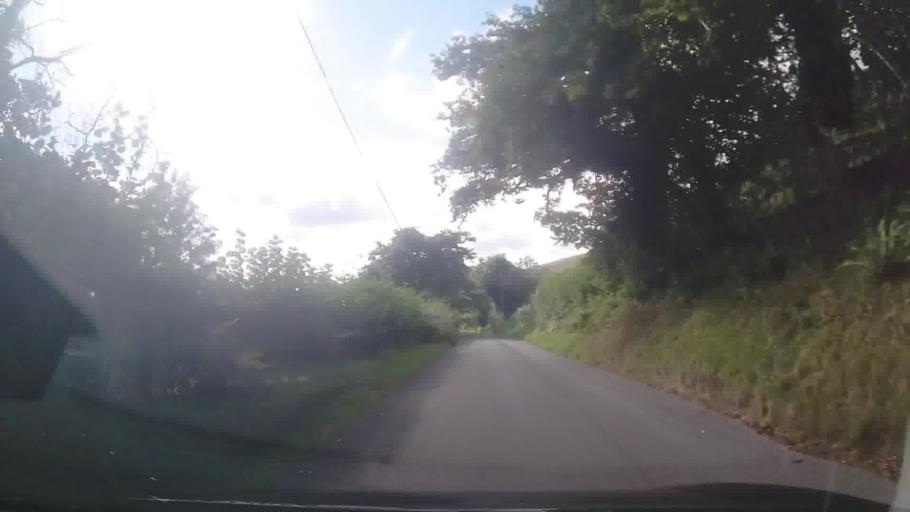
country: GB
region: Wales
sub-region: Gwynedd
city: Bala
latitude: 52.7509
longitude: -3.6365
